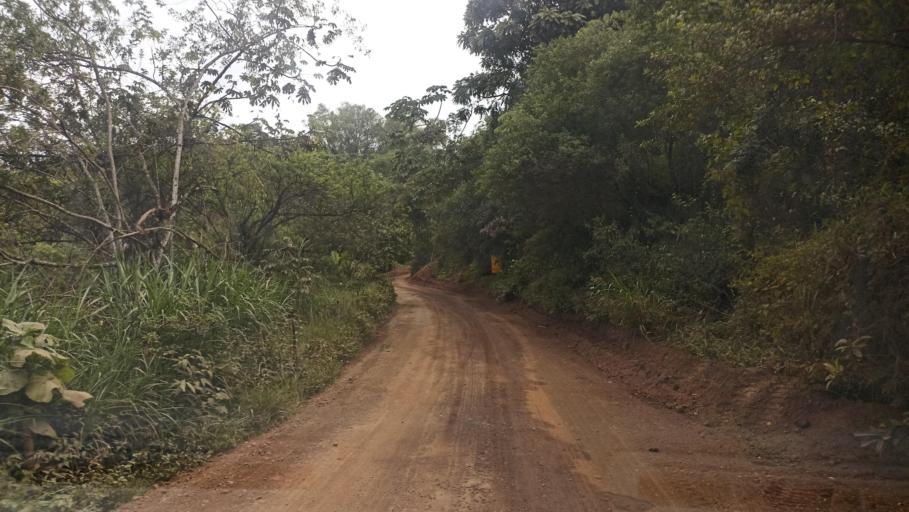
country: BR
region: Minas Gerais
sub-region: Congonhas
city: Congonhas
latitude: -20.4337
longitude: -43.7706
